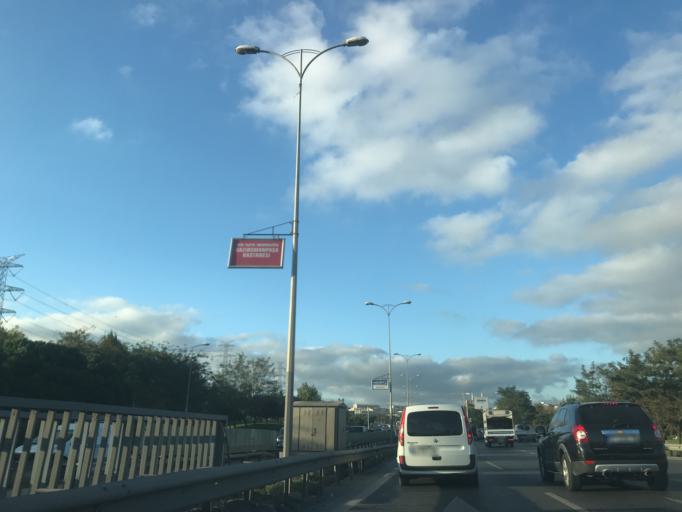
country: TR
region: Istanbul
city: Esenler
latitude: 41.0561
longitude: 28.8860
